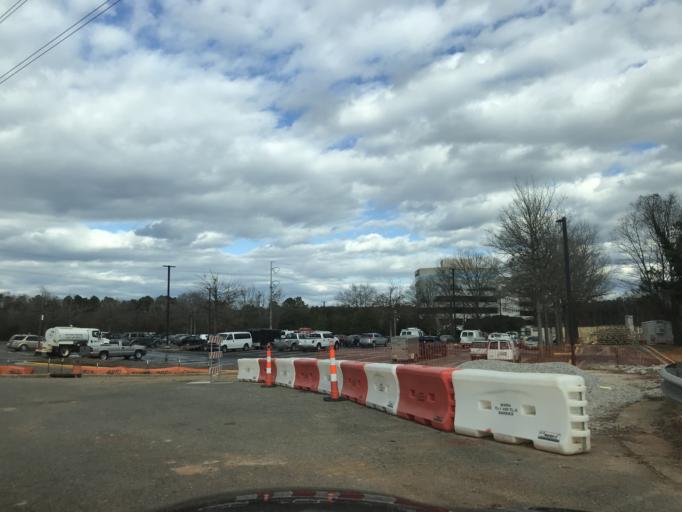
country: US
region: North Carolina
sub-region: Wake County
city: Cary
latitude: 35.7663
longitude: -78.7292
